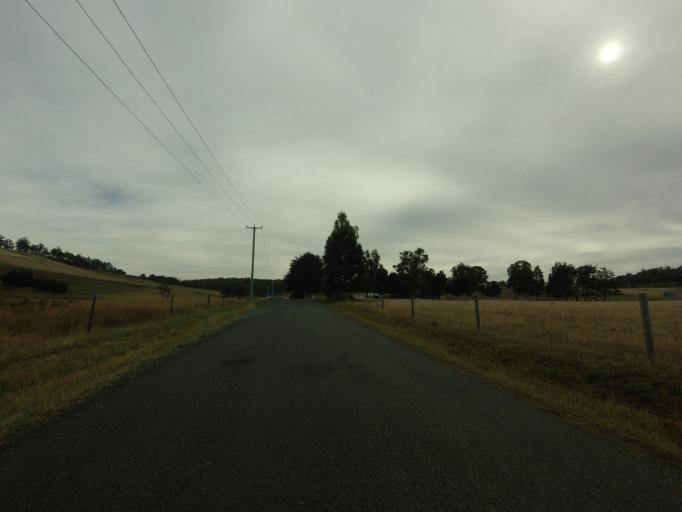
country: AU
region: Tasmania
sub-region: Sorell
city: Sorell
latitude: -42.4835
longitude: 147.5758
